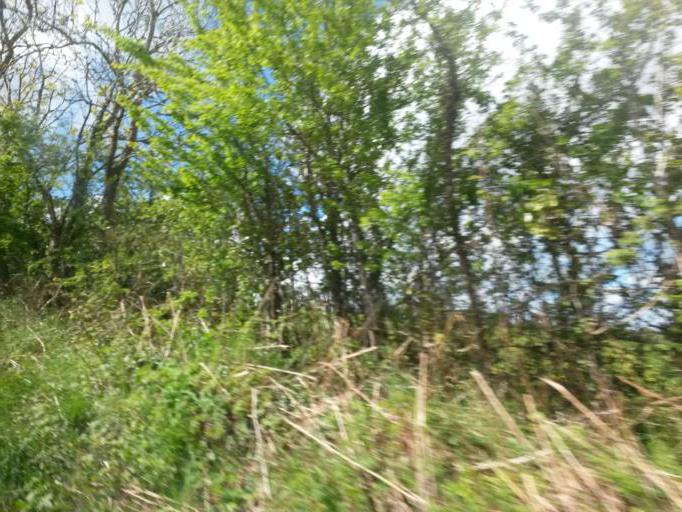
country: IE
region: Leinster
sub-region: Loch Garman
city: Castlebridge
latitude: 52.3752
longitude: -6.5038
